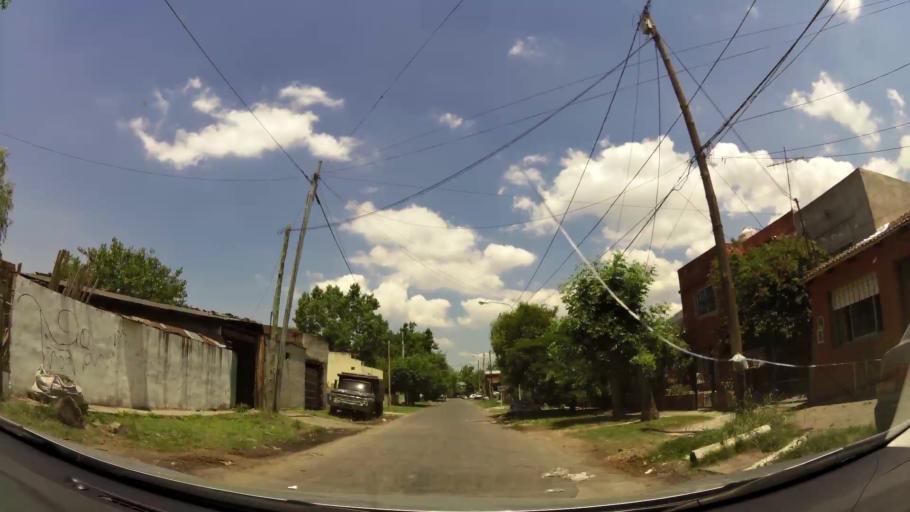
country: AR
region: Buenos Aires
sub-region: Partido de Tigre
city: Tigre
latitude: -34.4118
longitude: -58.5963
